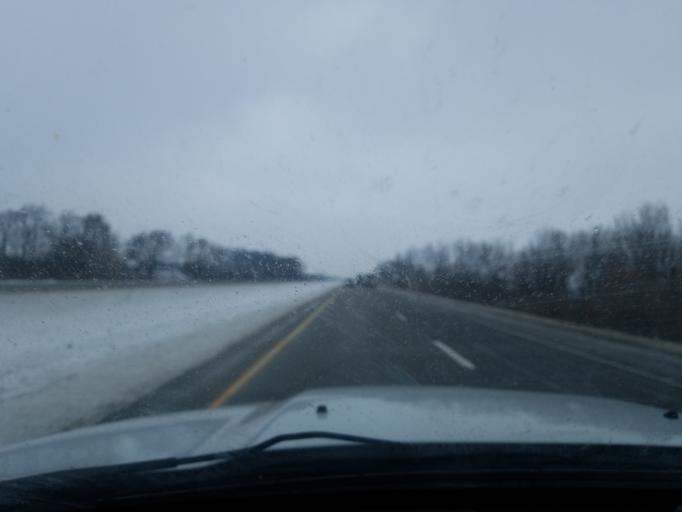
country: US
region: Indiana
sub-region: Marshall County
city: Argos
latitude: 41.1749
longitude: -86.2431
